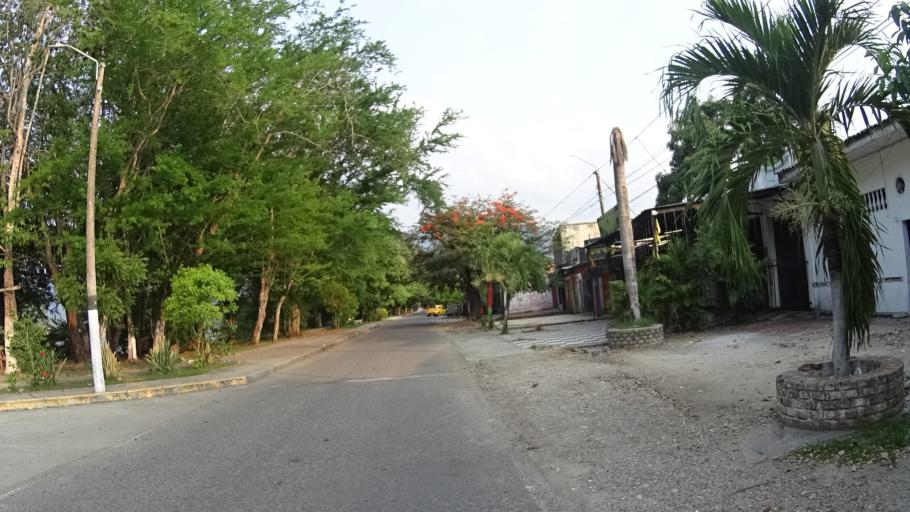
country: CO
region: Caldas
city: La Dorada
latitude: 5.4489
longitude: -74.6605
